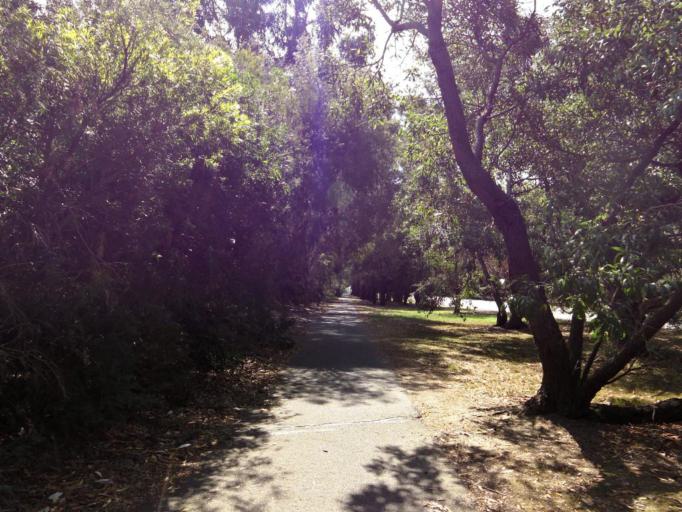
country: AU
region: Victoria
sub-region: Mornington Peninsula
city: Tyabb
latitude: -38.2356
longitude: 145.1863
